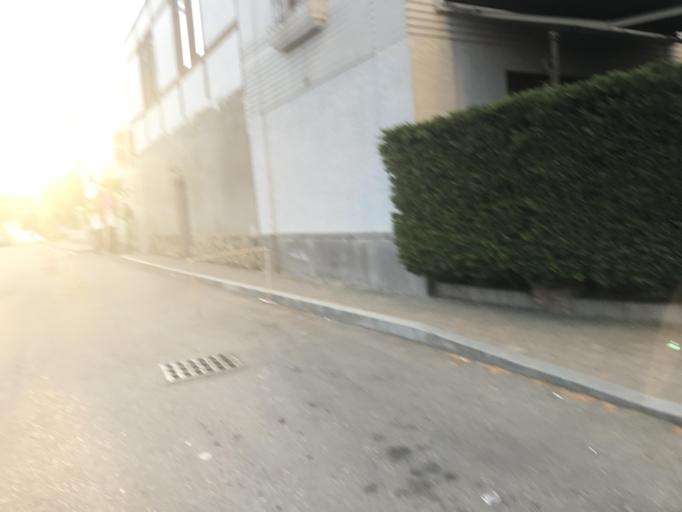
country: GE
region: Samegrelo and Zemo Svaneti
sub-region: Zugdidis Munitsip'alit'et'i
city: Zugdidi
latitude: 42.5068
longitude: 41.8733
